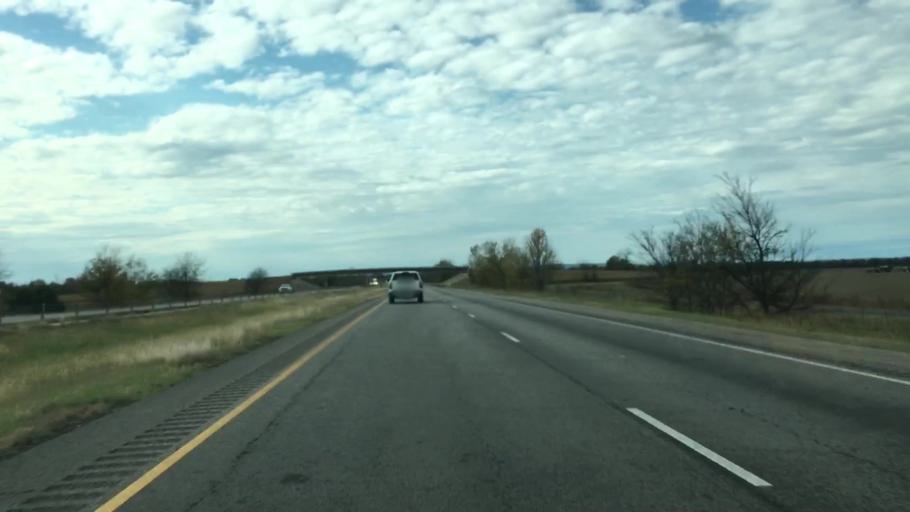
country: US
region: Arkansas
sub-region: Conway County
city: Morrilton
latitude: 35.1901
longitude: -92.7846
